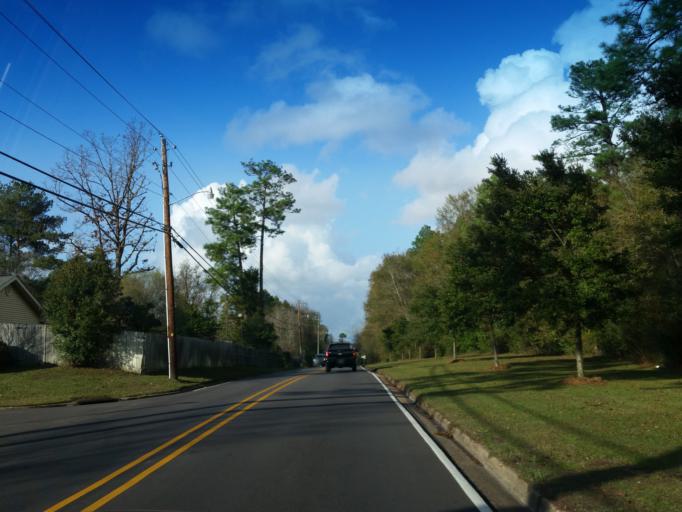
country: US
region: Mississippi
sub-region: Lamar County
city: West Hattiesburg
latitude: 31.3128
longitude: -89.3480
